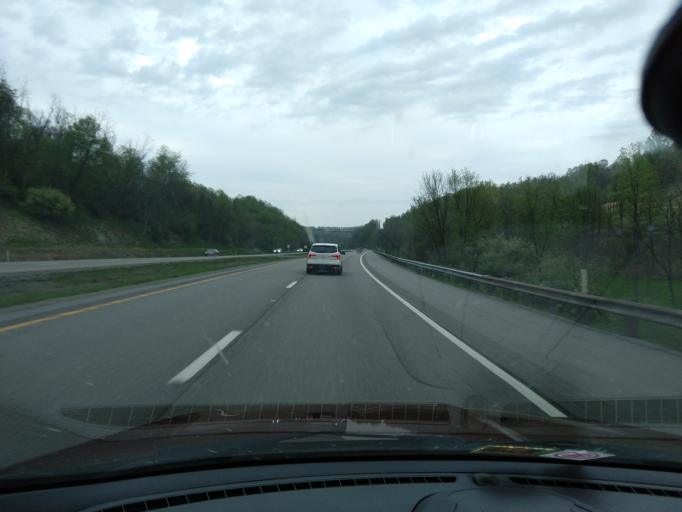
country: US
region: West Virginia
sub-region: Lewis County
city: Weston
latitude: 39.0609
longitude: -80.4017
